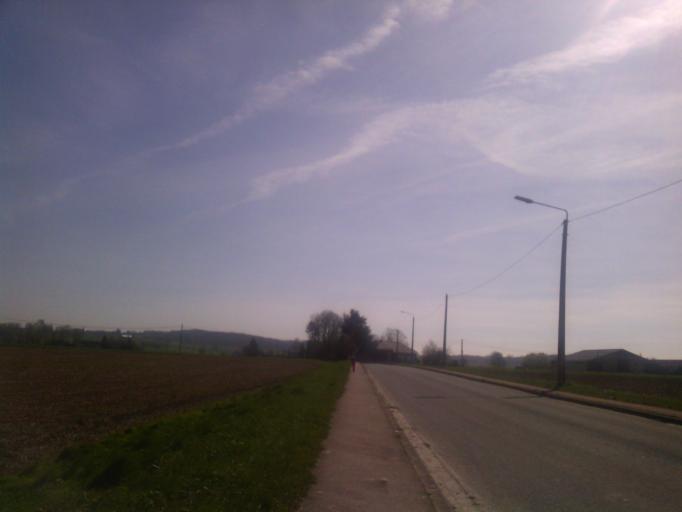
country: BE
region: Wallonia
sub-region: Province du Hainaut
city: Silly
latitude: 50.6606
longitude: 3.9367
